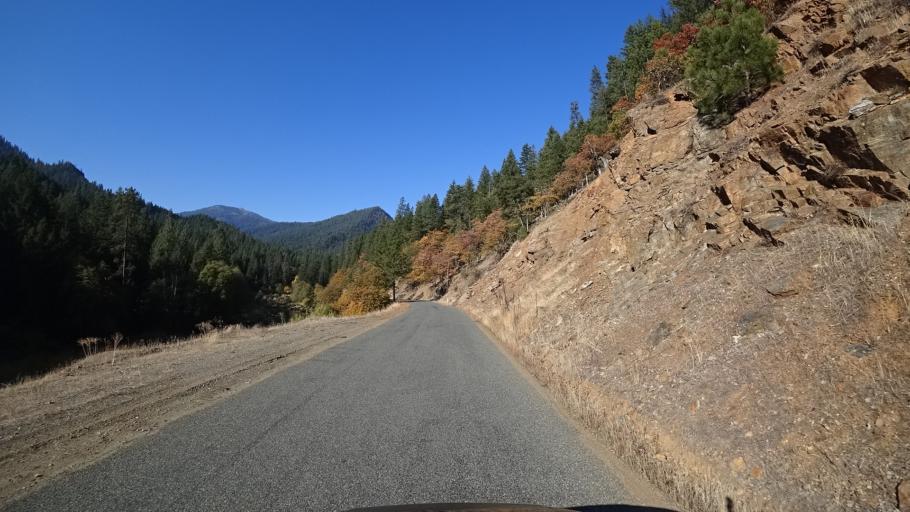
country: US
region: California
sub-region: Siskiyou County
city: Happy Camp
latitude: 41.6344
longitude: -123.0886
